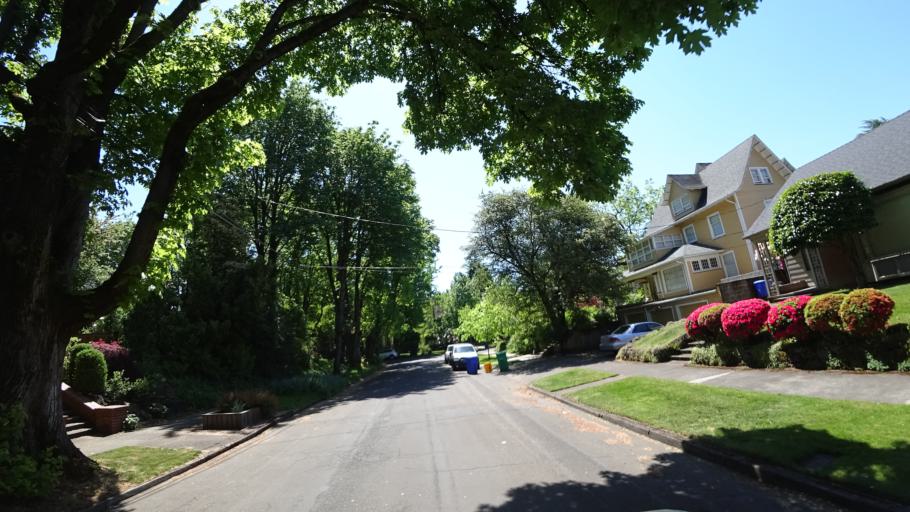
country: US
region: Oregon
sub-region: Multnomah County
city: Portland
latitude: 45.5380
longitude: -122.6423
